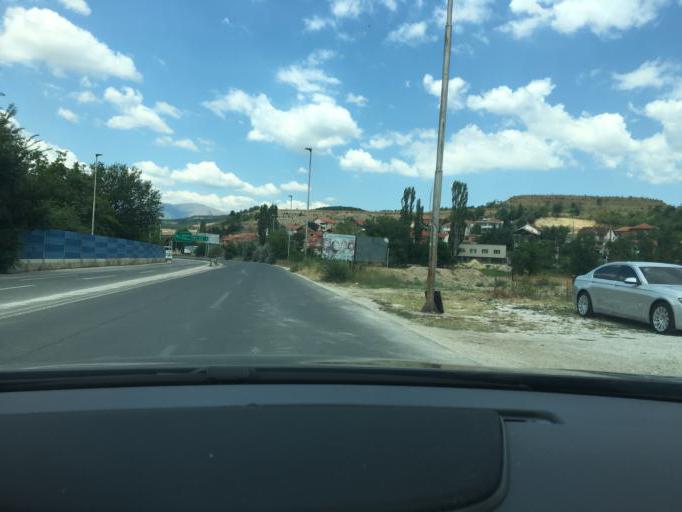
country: MK
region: Saraj
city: Saraj
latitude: 42.0076
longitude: 21.3297
